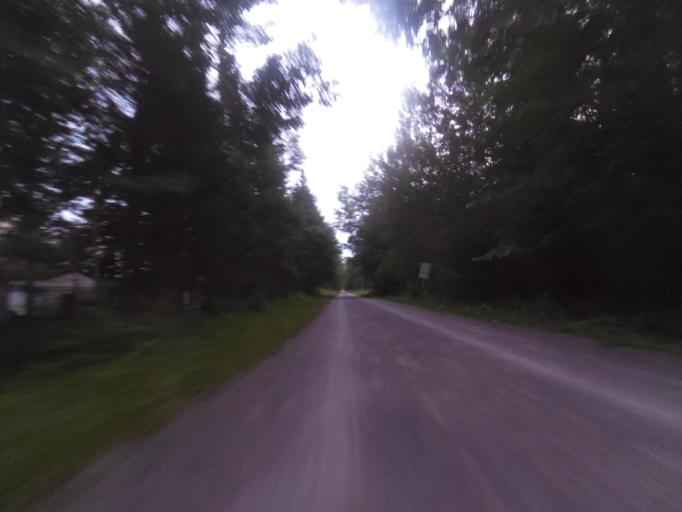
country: CA
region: Ontario
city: Bells Corners
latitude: 45.3018
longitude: -75.8605
